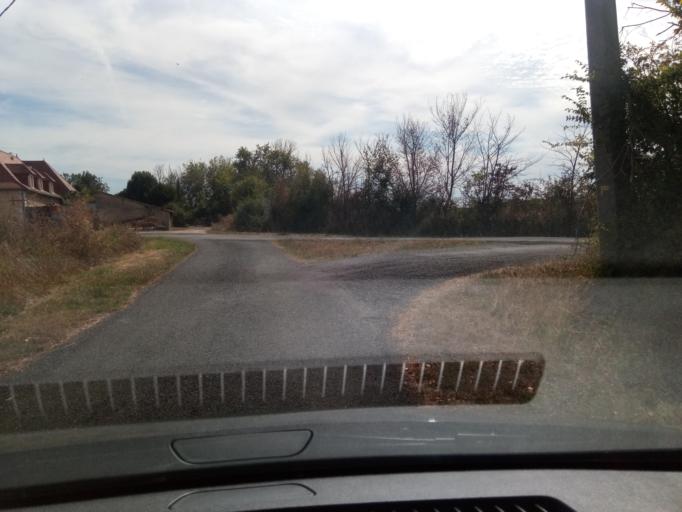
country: FR
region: Poitou-Charentes
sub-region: Departement de la Vienne
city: Chauvigny
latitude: 46.5551
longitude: 0.7394
